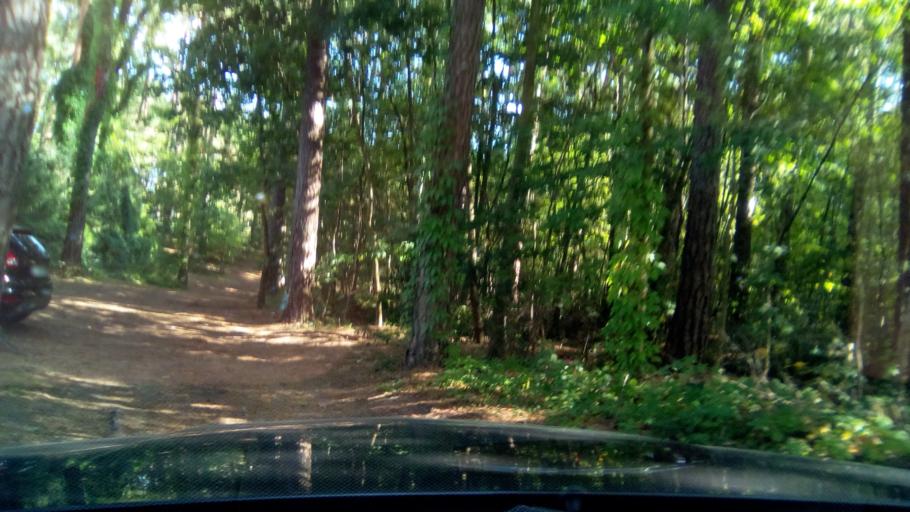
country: PL
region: West Pomeranian Voivodeship
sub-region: Powiat szczecinecki
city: Borne Sulinowo
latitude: 53.5899
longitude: 16.5431
